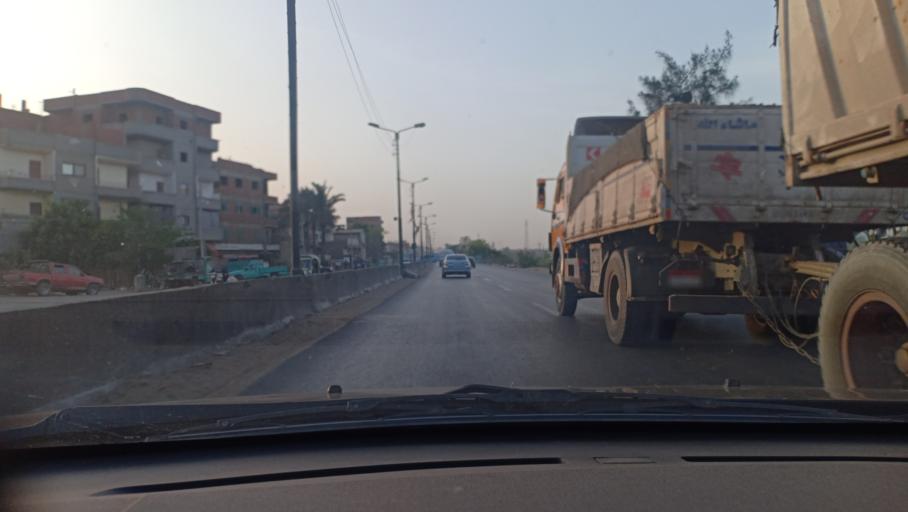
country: EG
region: Muhafazat al Gharbiyah
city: Zifta
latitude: 30.6840
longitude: 31.2808
